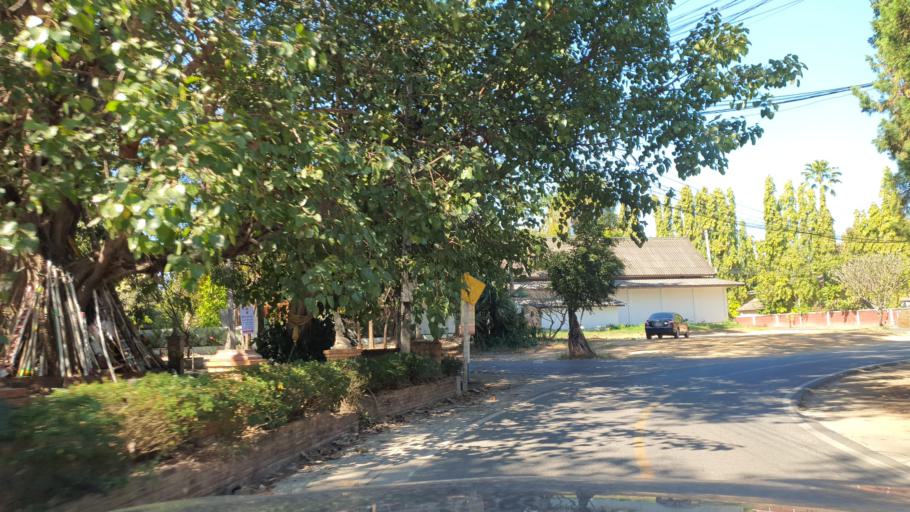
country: TH
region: Chiang Mai
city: Hang Dong
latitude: 18.6823
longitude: 98.9207
